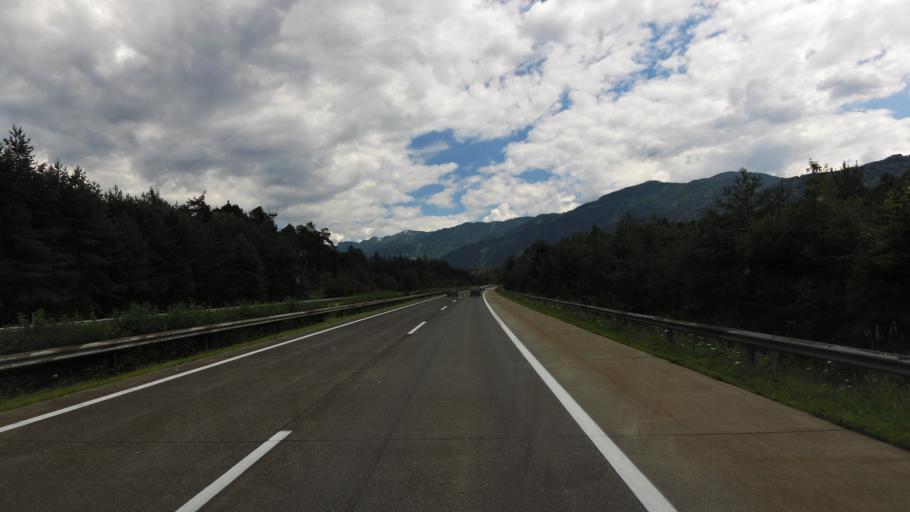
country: AT
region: Carinthia
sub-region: Politischer Bezirk Villach Land
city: Arnoldstein
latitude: 46.5647
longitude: 13.7380
